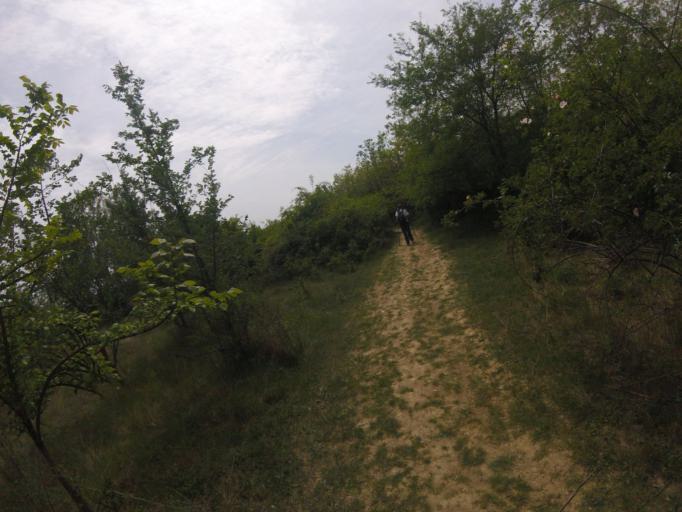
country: HU
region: Pest
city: Telki
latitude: 47.5551
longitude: 18.8322
